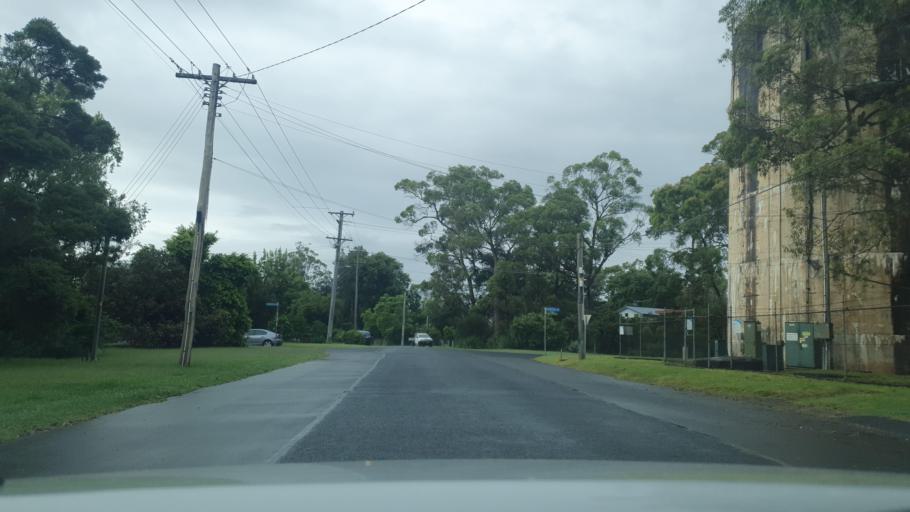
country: AU
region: New South Wales
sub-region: Blue Mountains Municipality
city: Glenbrook
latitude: -33.7746
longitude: 150.6284
